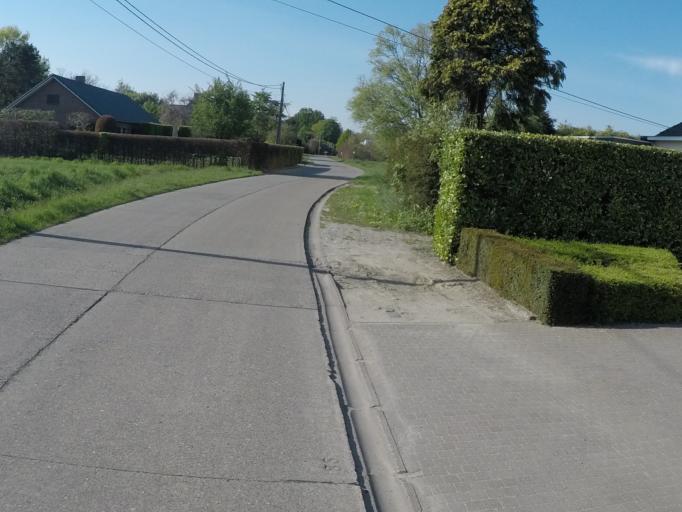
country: BE
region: Flanders
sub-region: Provincie Antwerpen
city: Nijlen
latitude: 51.1506
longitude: 4.6367
